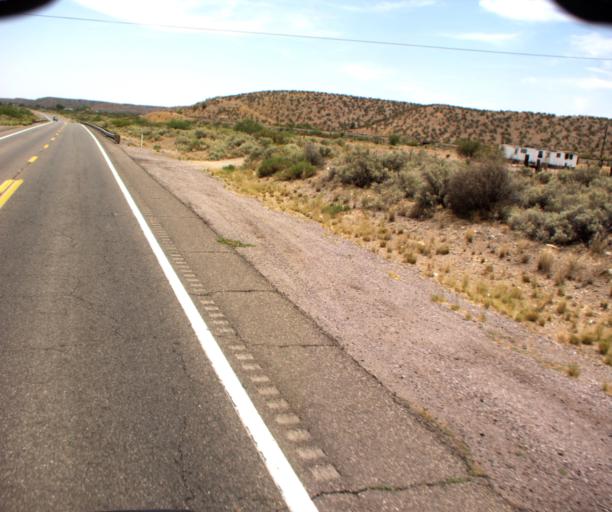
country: US
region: Arizona
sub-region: Graham County
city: Bylas
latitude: 33.0991
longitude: -110.0783
